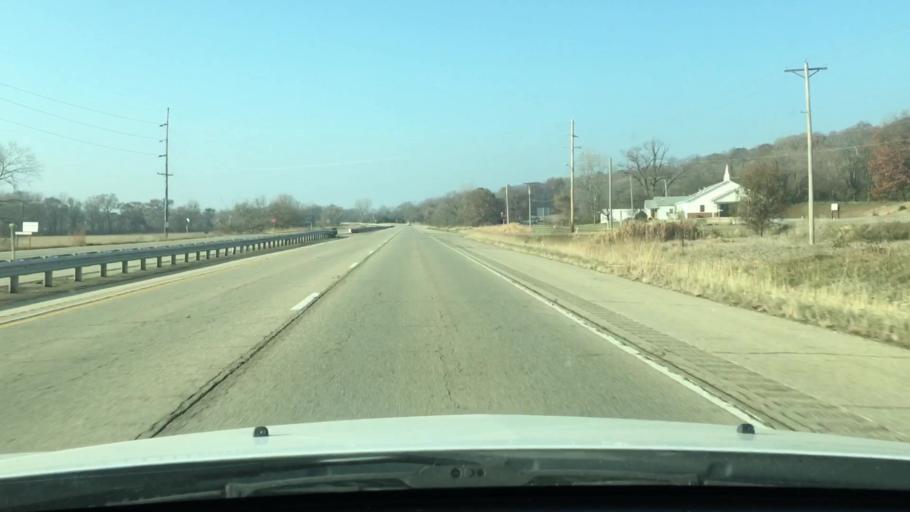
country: US
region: Illinois
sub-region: Tazewell County
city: Pekin
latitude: 40.5761
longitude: -89.7076
